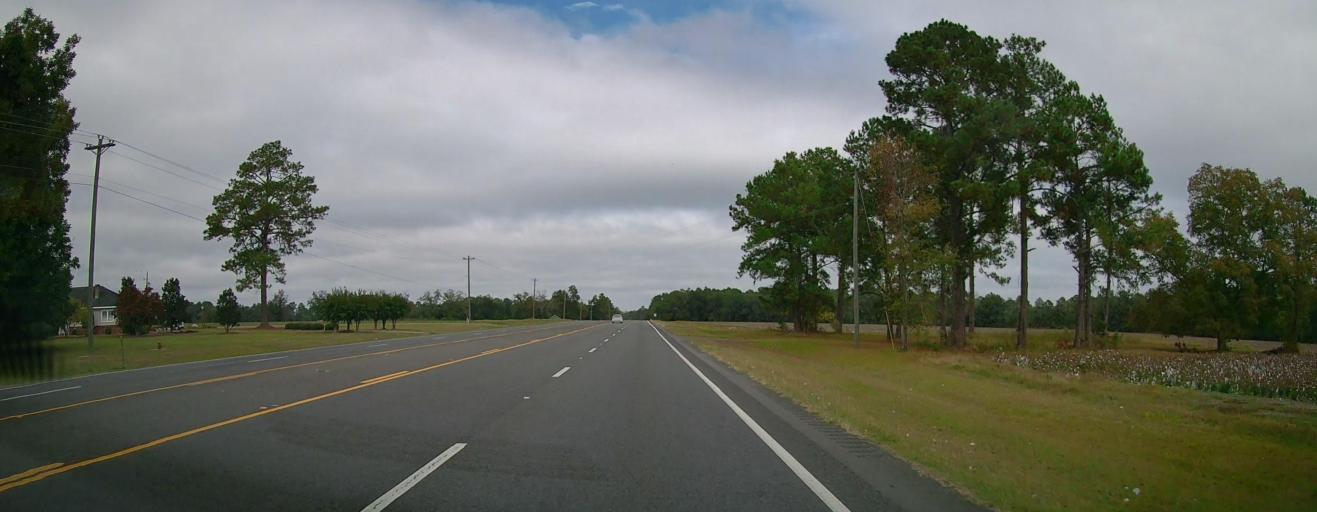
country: US
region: Georgia
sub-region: Thomas County
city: Thomasville
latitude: 30.9939
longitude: -83.8743
